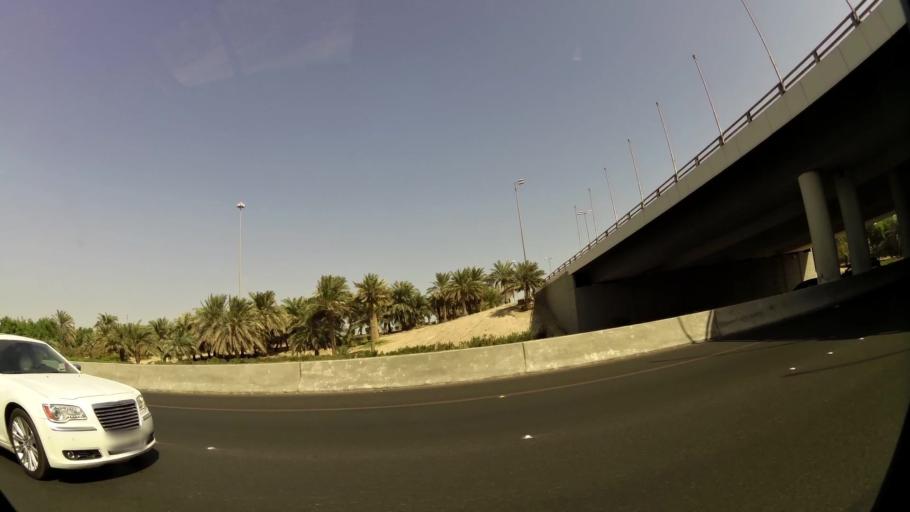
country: KW
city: Bayan
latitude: 29.2798
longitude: 48.0349
